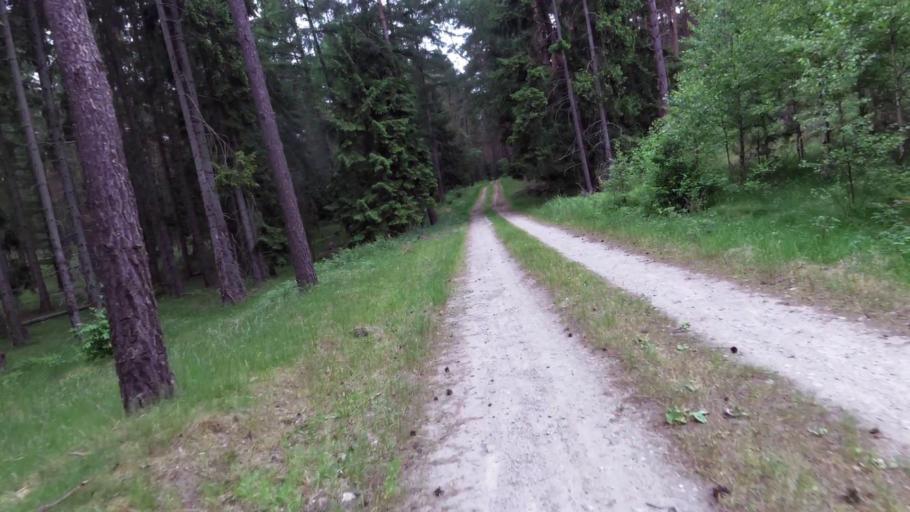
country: PL
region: West Pomeranian Voivodeship
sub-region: Powiat mysliborski
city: Debno
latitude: 52.8212
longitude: 14.6481
